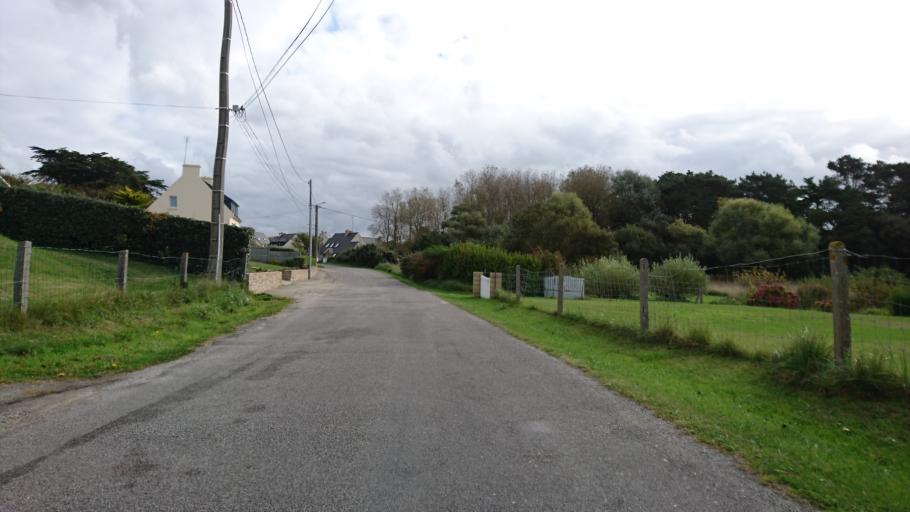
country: FR
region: Brittany
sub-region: Departement du Finistere
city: Lampaul-Plouarzel
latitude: 48.4446
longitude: -4.7738
